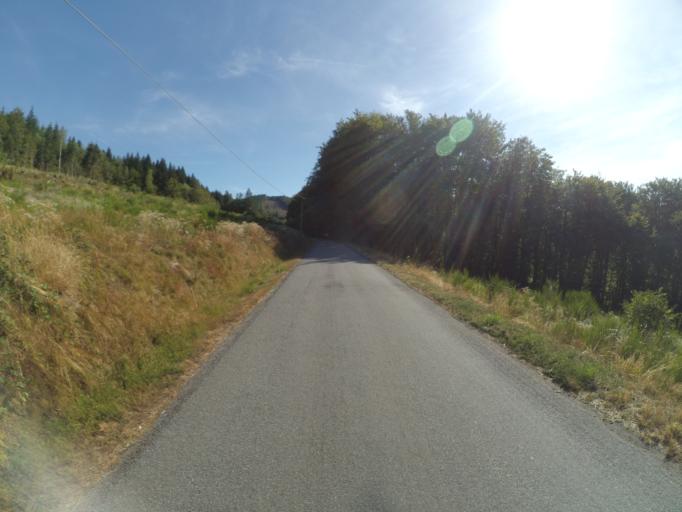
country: FR
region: Limousin
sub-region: Departement de la Correze
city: Bugeat
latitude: 45.6853
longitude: 1.9573
